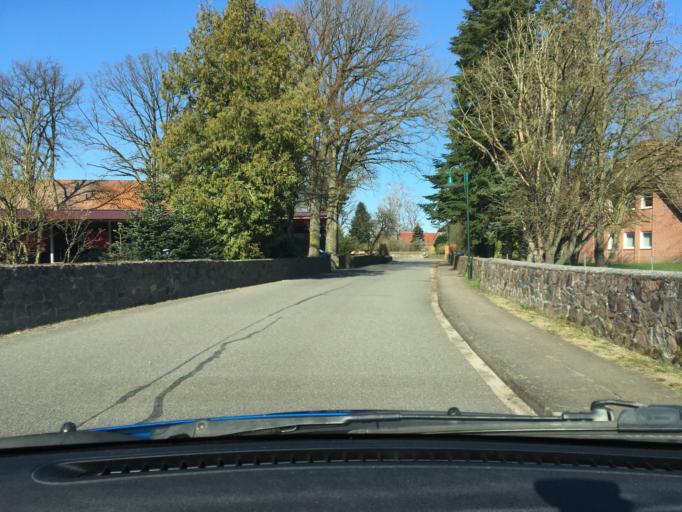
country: DE
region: Lower Saxony
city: Embsen
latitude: 53.1766
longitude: 10.3415
